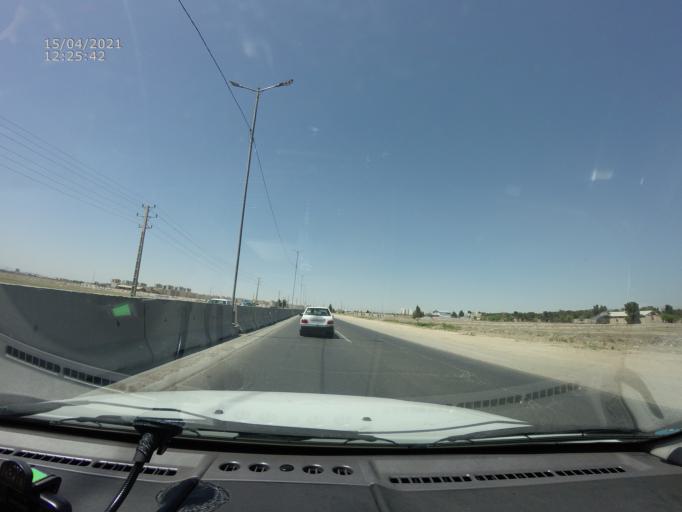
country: IR
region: Tehran
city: Eslamshahr
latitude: 35.5125
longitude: 51.2423
